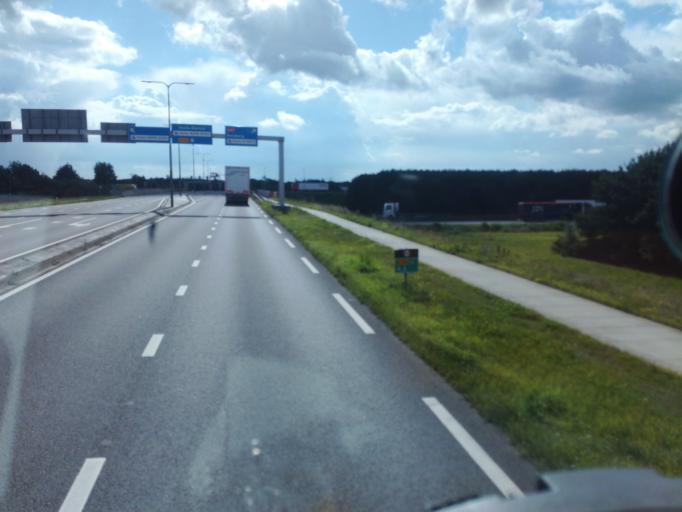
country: NL
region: Limburg
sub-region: Gemeente Peel en Maas
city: Maasbree
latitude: 51.3955
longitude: 6.0835
